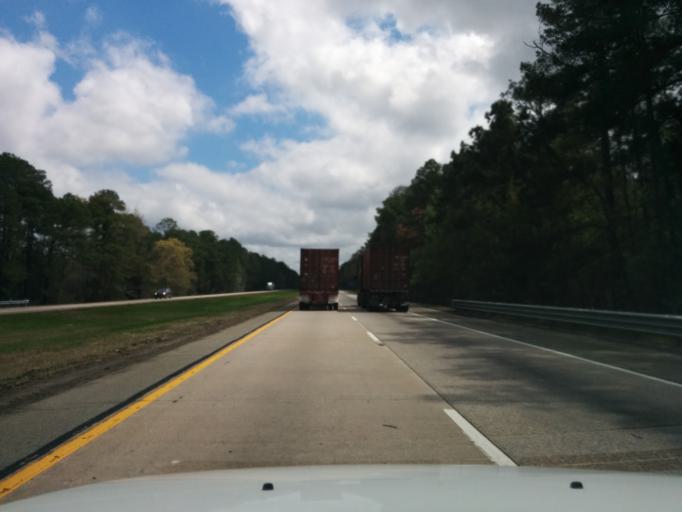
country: US
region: Georgia
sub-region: Bryan County
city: Pembroke
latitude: 32.1968
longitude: -81.4809
